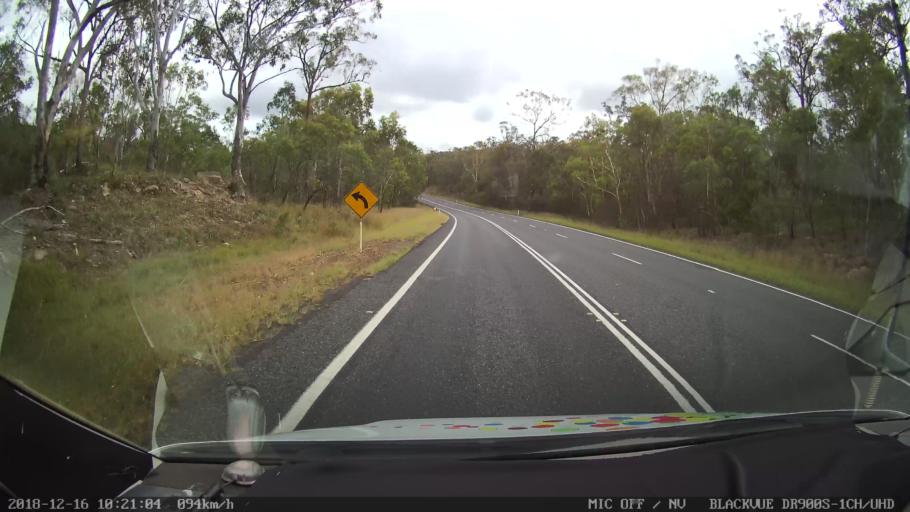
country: AU
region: New South Wales
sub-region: Tenterfield Municipality
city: Carrolls Creek
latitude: -29.2121
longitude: 152.0123
